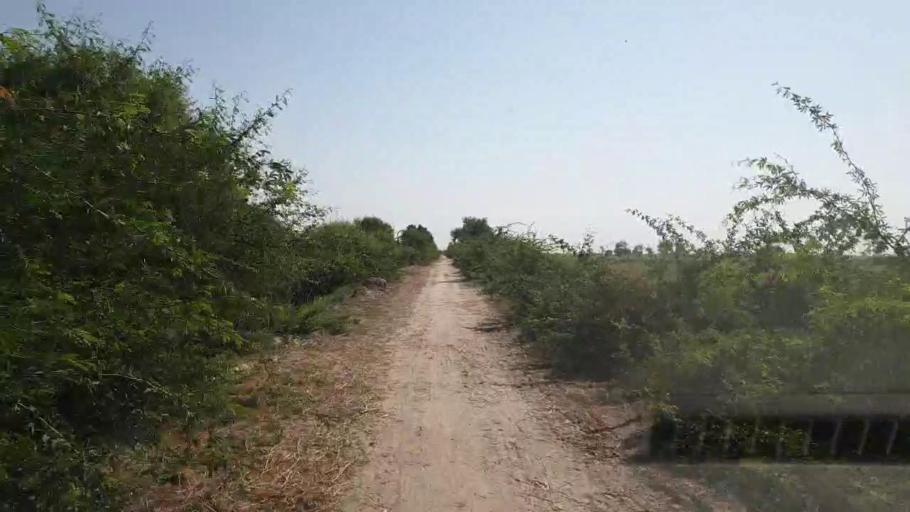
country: PK
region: Sindh
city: Kadhan
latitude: 24.6223
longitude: 68.9957
